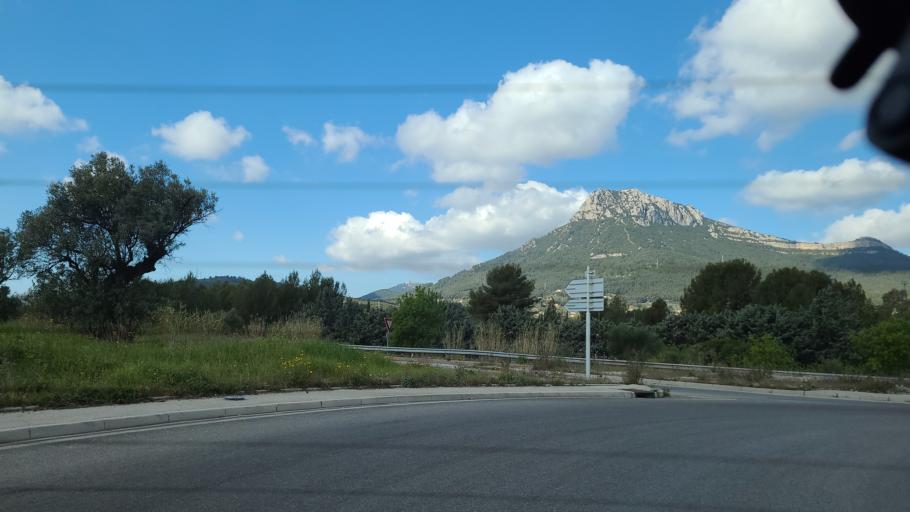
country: FR
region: Provence-Alpes-Cote d'Azur
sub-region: Departement du Var
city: La Farlede
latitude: 43.1582
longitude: 6.0447
